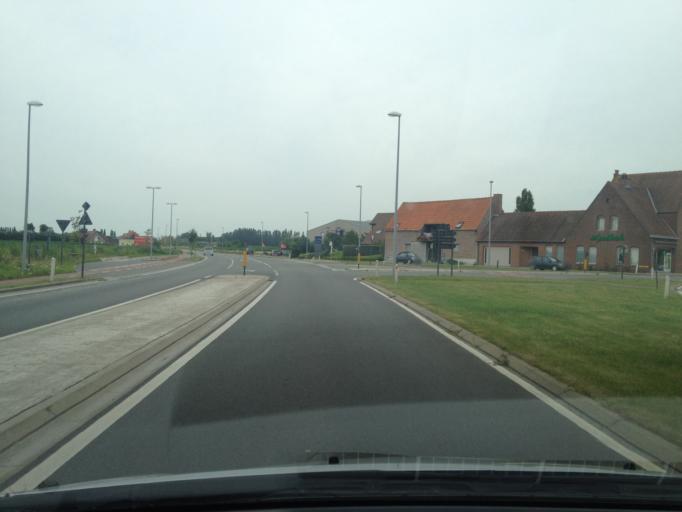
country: BE
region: Flanders
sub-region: Provincie West-Vlaanderen
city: Diksmuide
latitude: 51.0577
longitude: 2.8770
